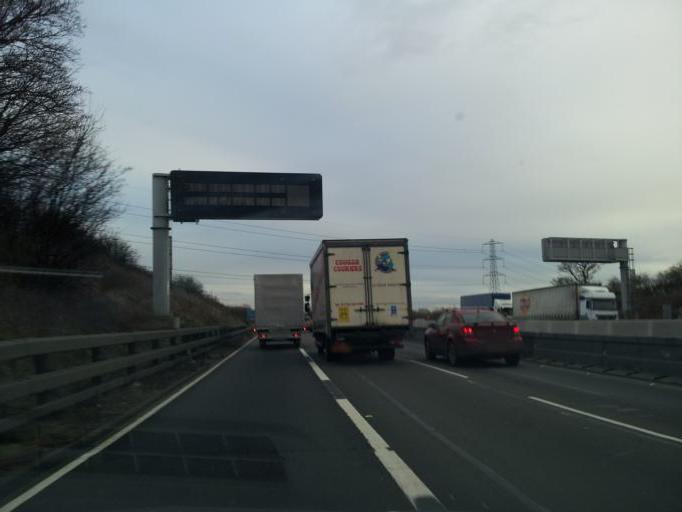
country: GB
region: England
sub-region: Northamptonshire
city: Bugbrooke
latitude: 52.2399
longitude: -1.0470
